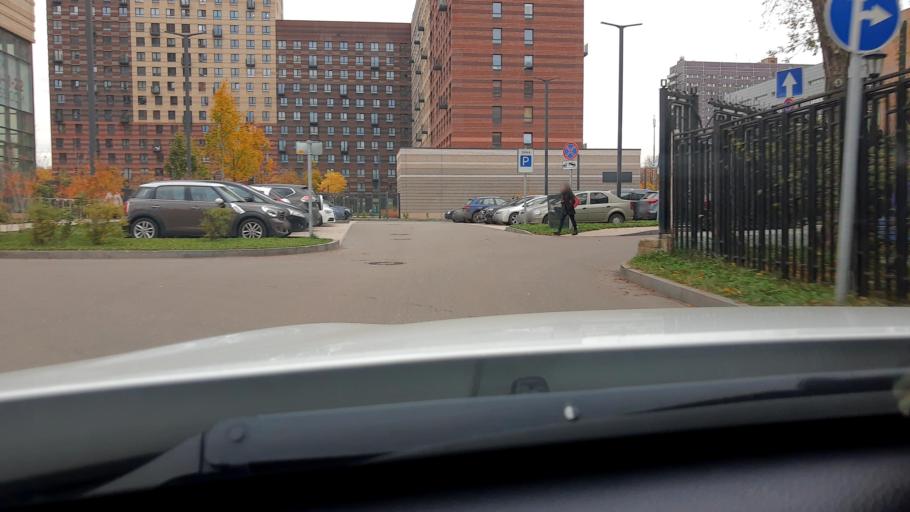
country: RU
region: Moscow
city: Sokol
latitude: 55.8077
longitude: 37.5397
